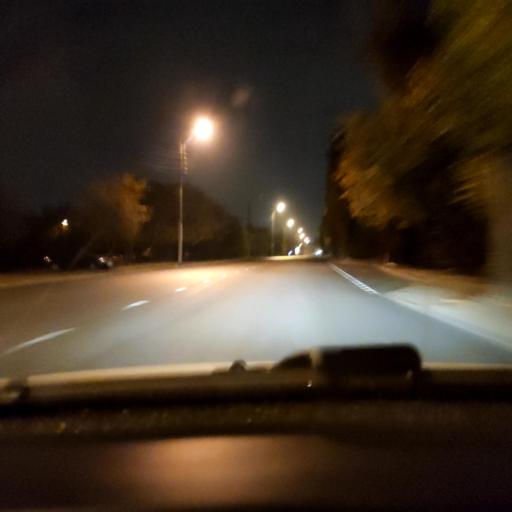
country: RU
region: Voronezj
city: Voronezh
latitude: 51.6211
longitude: 39.1761
